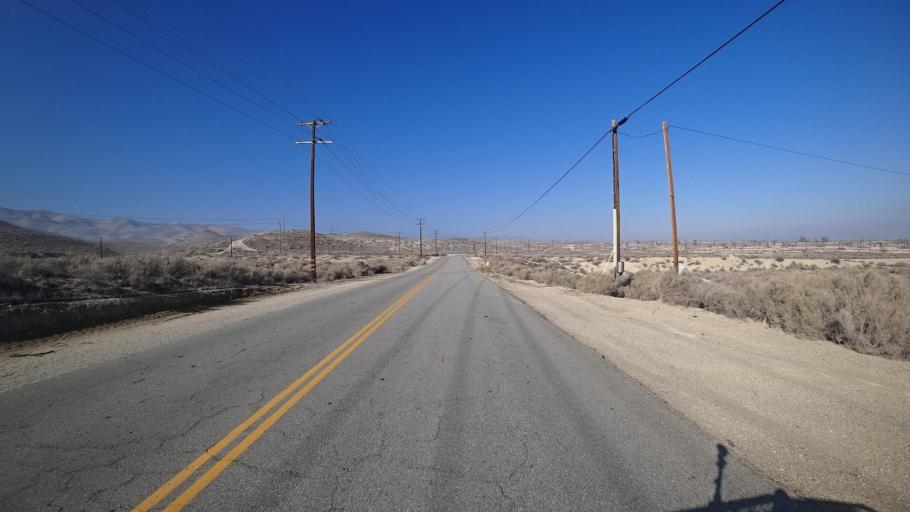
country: US
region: California
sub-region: Kern County
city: Taft Heights
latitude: 35.1959
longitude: -119.5861
